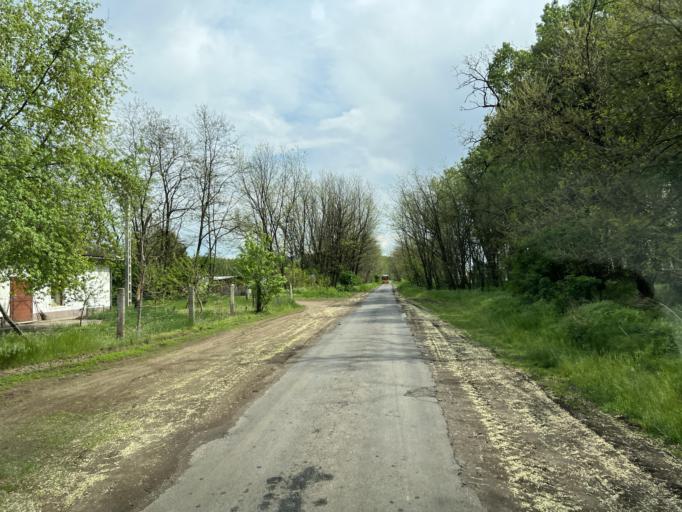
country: HU
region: Pest
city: Nagykoros
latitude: 46.9792
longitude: 19.8102
